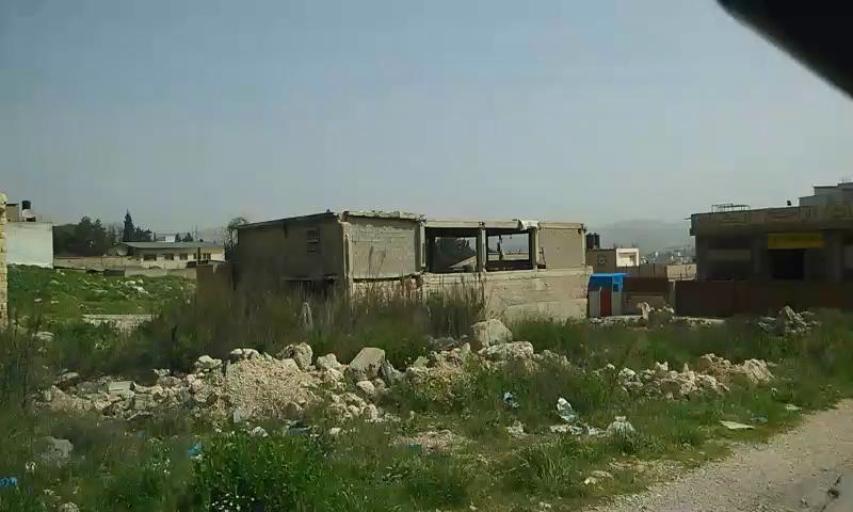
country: PS
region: West Bank
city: Balatah
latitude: 32.2154
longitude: 35.2902
